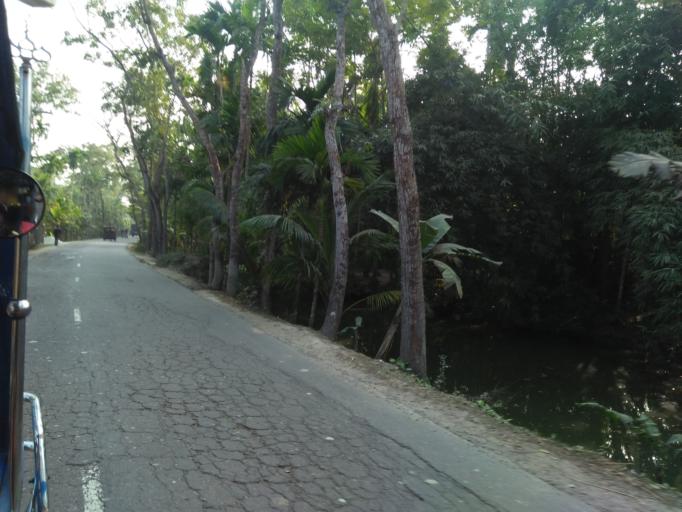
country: BD
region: Barisal
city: Bhola
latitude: 22.7101
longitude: 90.6402
